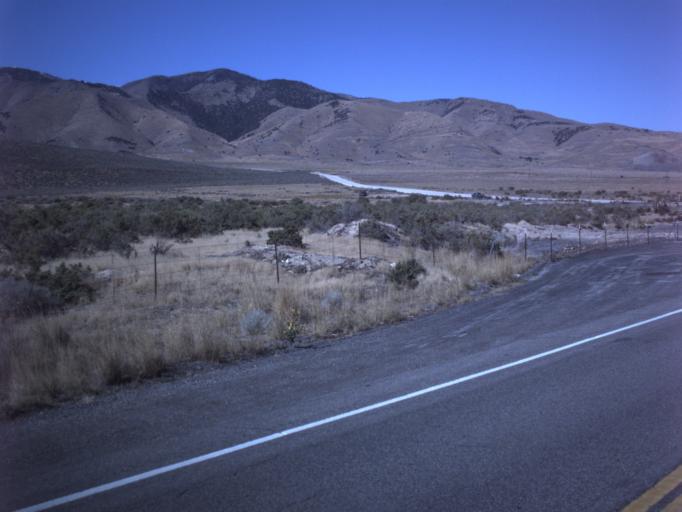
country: US
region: Utah
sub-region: Tooele County
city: Grantsville
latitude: 40.6391
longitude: -112.5225
